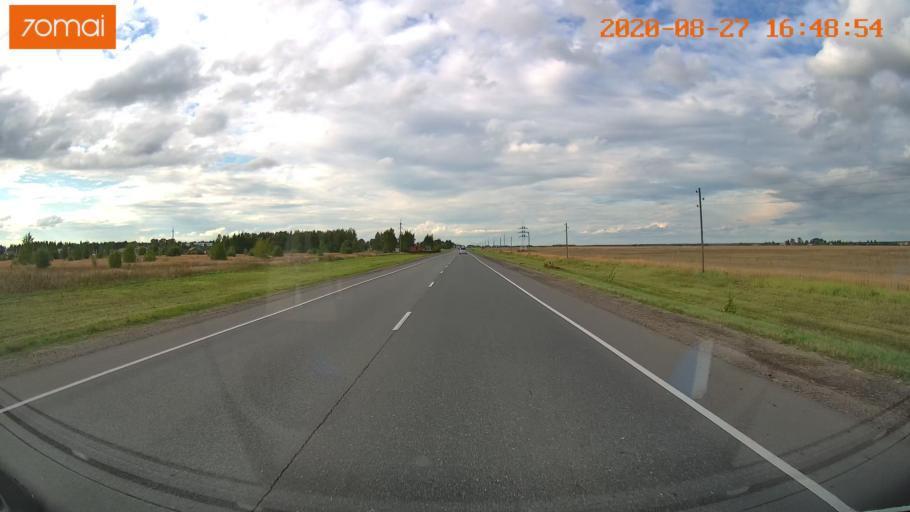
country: RU
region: Vladimir
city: Suzdal'
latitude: 56.4328
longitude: 40.4713
